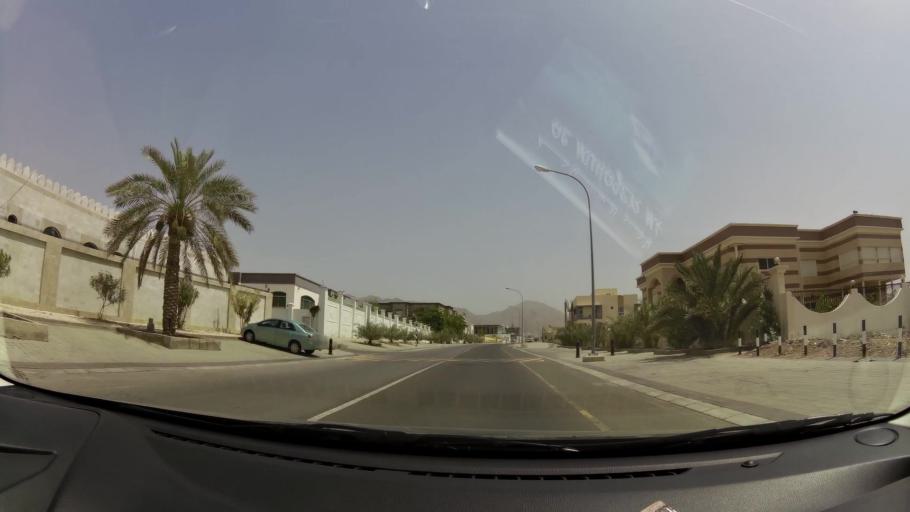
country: OM
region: Muhafazat Masqat
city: Bawshar
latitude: 23.5613
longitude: 58.3947
